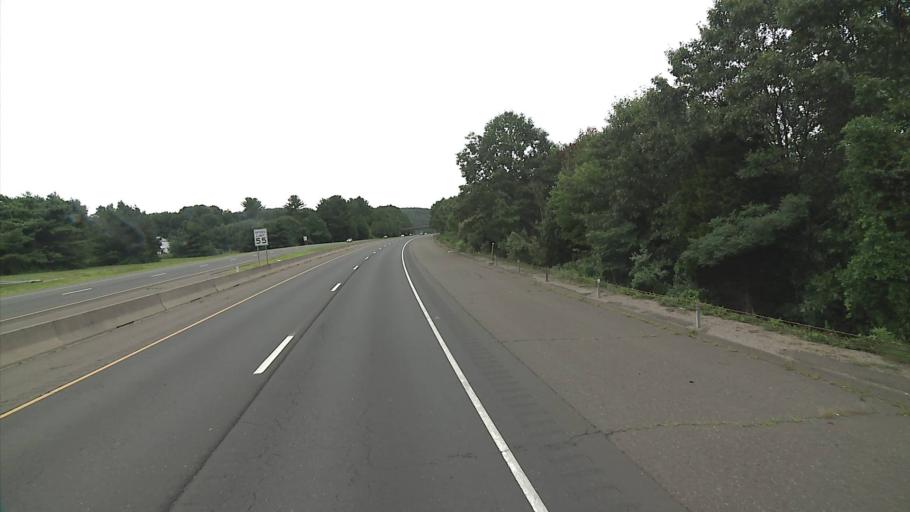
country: US
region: Connecticut
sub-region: New Haven County
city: Seymour
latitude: 41.4356
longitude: -73.0673
